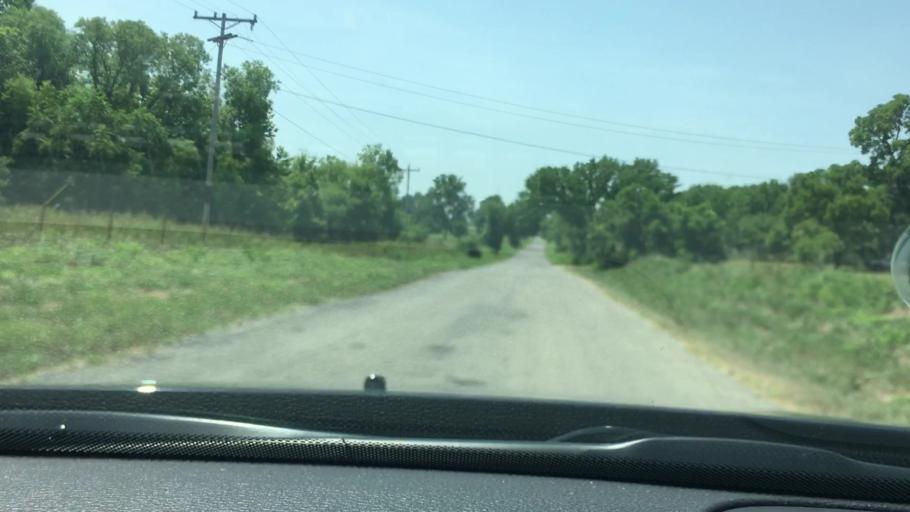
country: US
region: Oklahoma
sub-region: Pontotoc County
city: Byng
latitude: 34.8372
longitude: -96.6698
